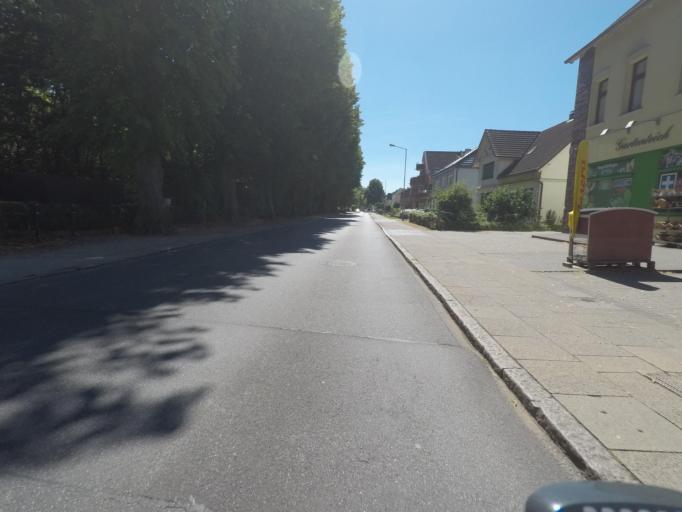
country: DE
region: Schleswig-Holstein
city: Trittau
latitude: 53.6180
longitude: 10.4028
